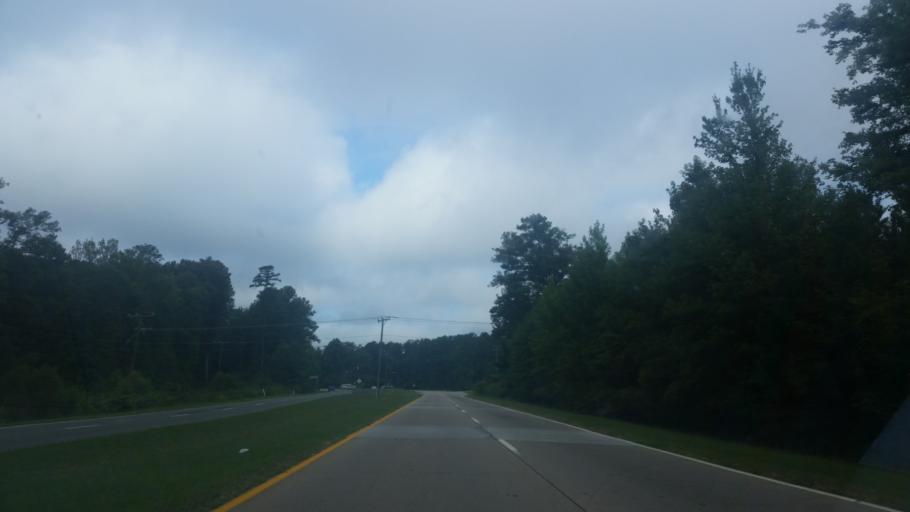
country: US
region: Virginia
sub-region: Henrico County
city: Sandston
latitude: 37.5128
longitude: -77.1958
